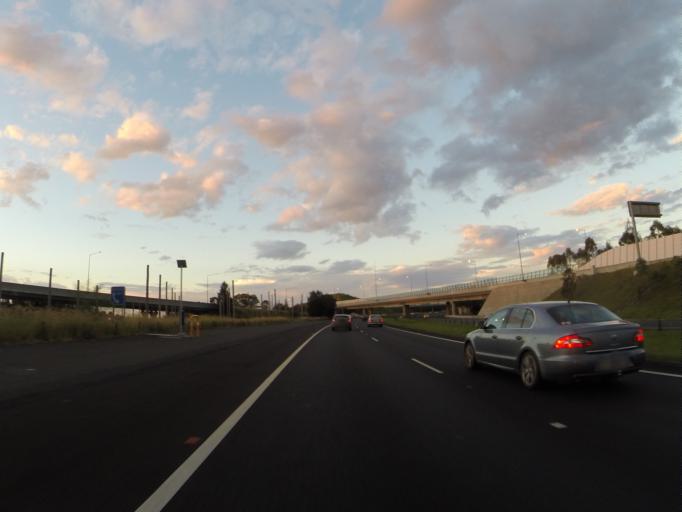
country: AU
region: New South Wales
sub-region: Campbelltown Municipality
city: Glenfield
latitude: -33.9545
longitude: 150.8773
